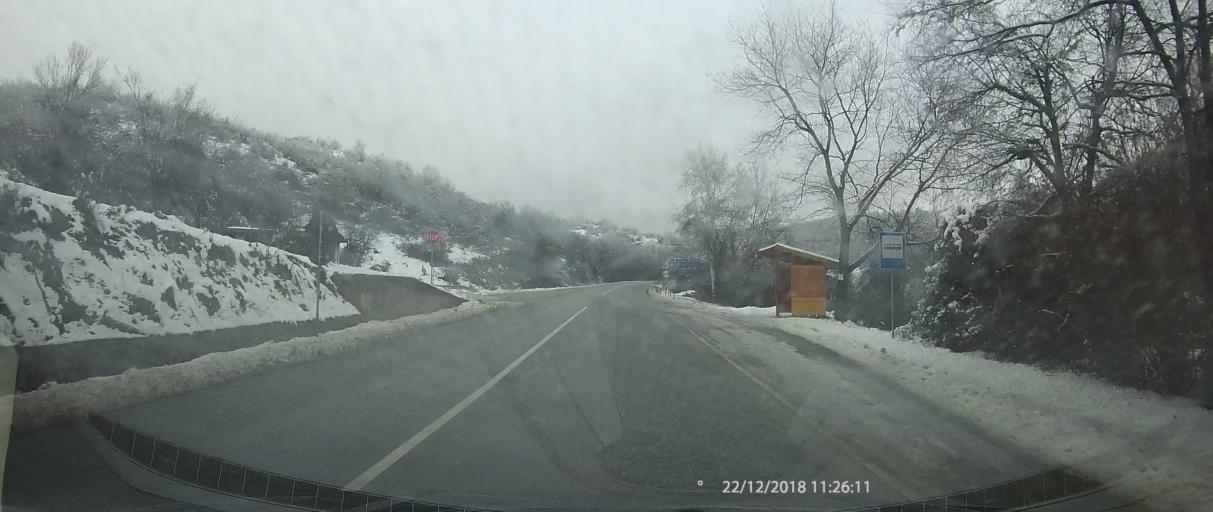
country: BG
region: Kyustendil
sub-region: Obshtina Boboshevo
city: Boboshevo
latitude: 42.2635
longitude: 22.9192
